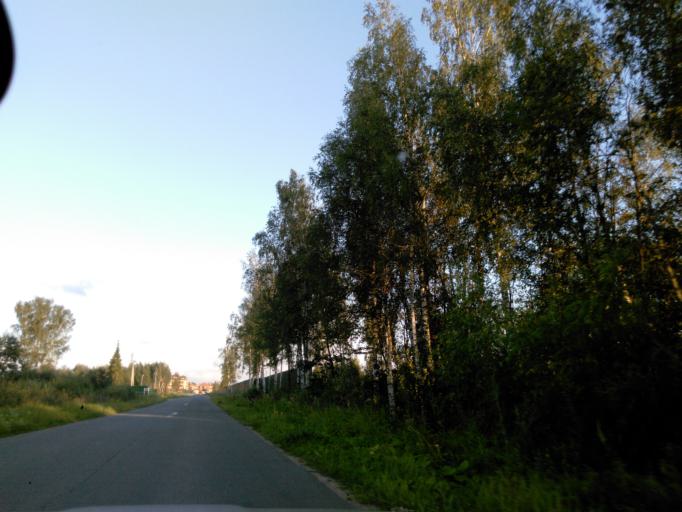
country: RU
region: Tverskaya
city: Konakovo
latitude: 56.6809
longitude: 36.7052
